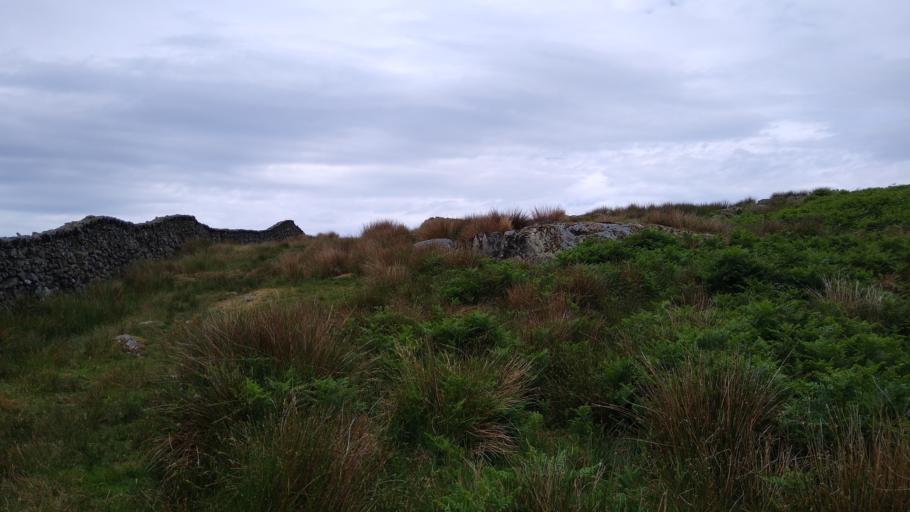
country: GB
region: England
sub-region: Cumbria
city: Millom
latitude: 54.2877
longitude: -3.2612
